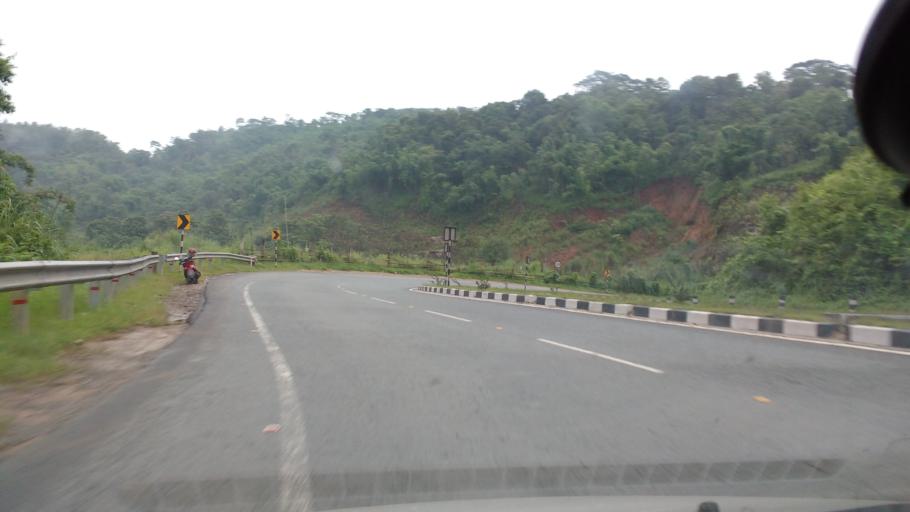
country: IN
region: Meghalaya
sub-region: Ri-Bhoi
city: Nongpoh
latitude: 25.7871
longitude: 91.8715
